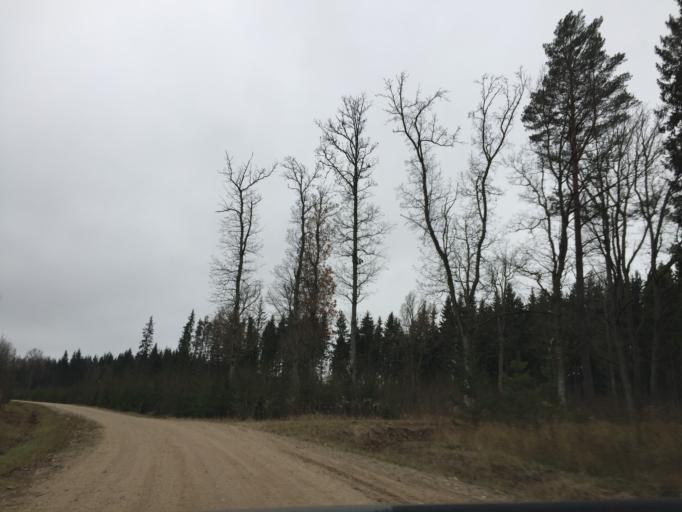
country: LV
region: Limbazu Rajons
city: Limbazi
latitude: 57.4921
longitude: 24.7666
